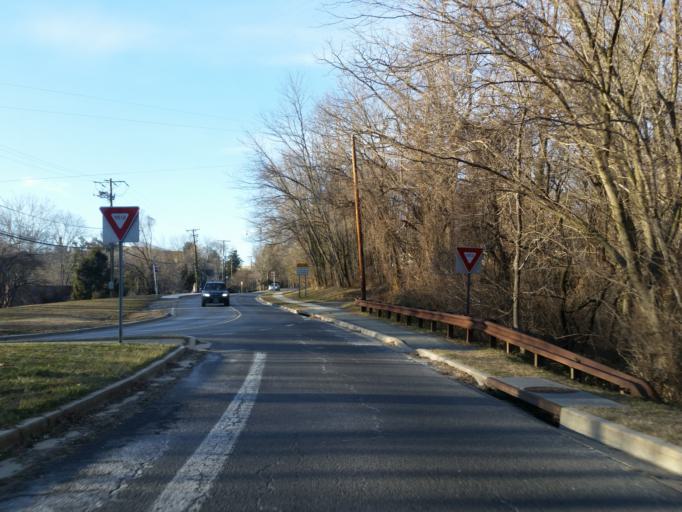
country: US
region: Maryland
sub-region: Montgomery County
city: Brookmont
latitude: 38.9444
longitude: -77.1167
